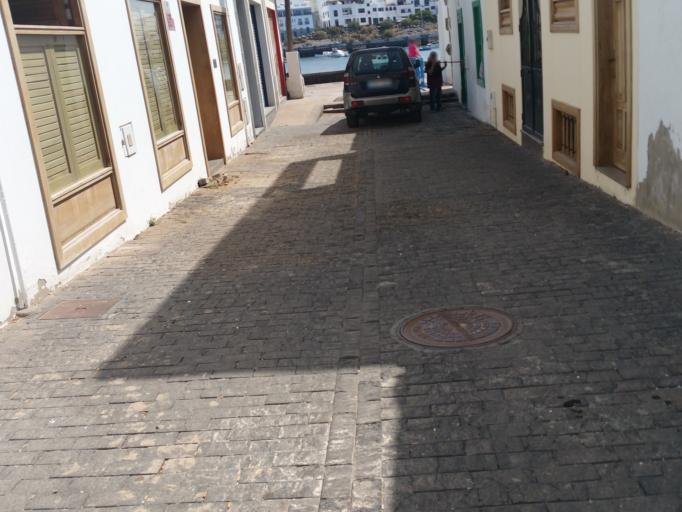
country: ES
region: Canary Islands
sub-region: Provincia de Las Palmas
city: Arrecife
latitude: 28.9601
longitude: -13.5478
